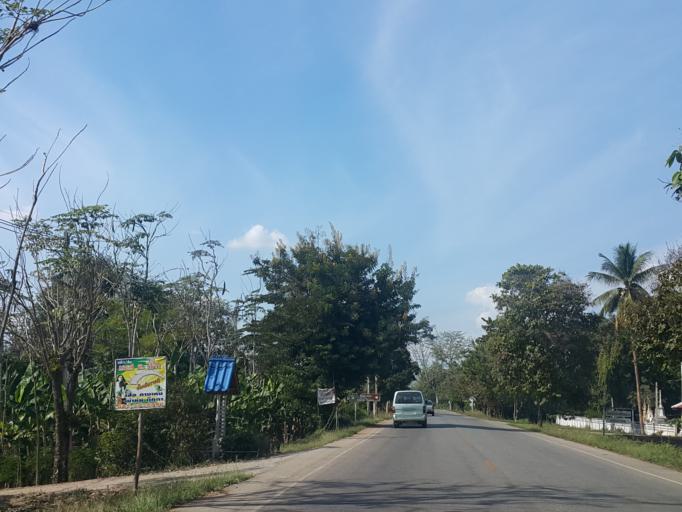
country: TH
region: Sukhothai
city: Sawankhalok
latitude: 17.2527
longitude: 99.8435
